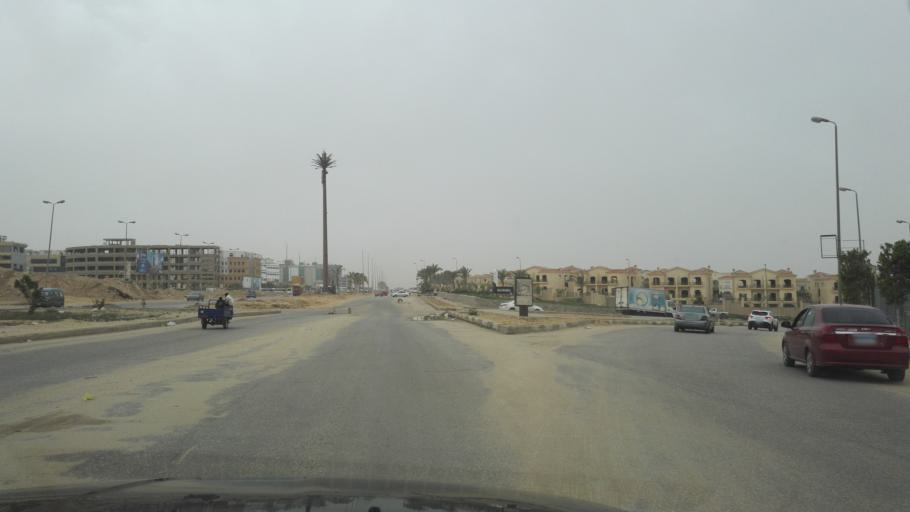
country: EG
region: Muhafazat al Qalyubiyah
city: Al Khankah
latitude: 30.0289
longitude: 31.4969
